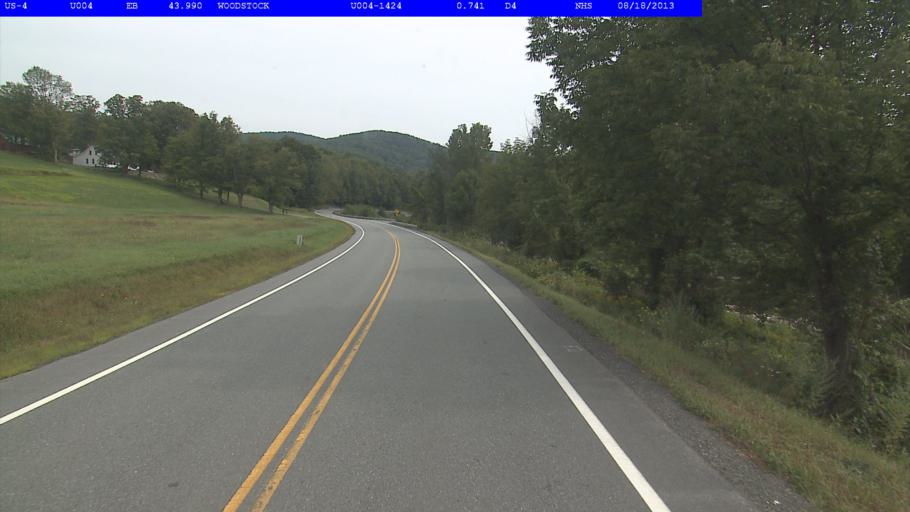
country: US
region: Vermont
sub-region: Windsor County
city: Woodstock
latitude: 43.5911
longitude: -72.6086
